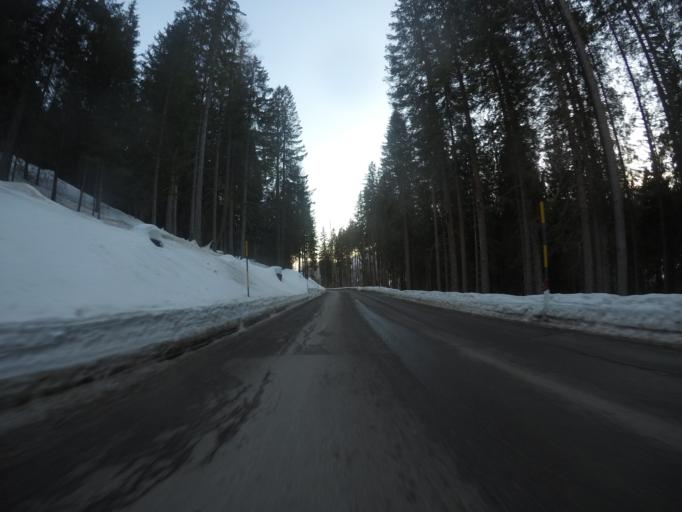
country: IT
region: Trentino-Alto Adige
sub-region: Provincia di Trento
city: Siror
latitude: 46.2688
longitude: 11.8044
